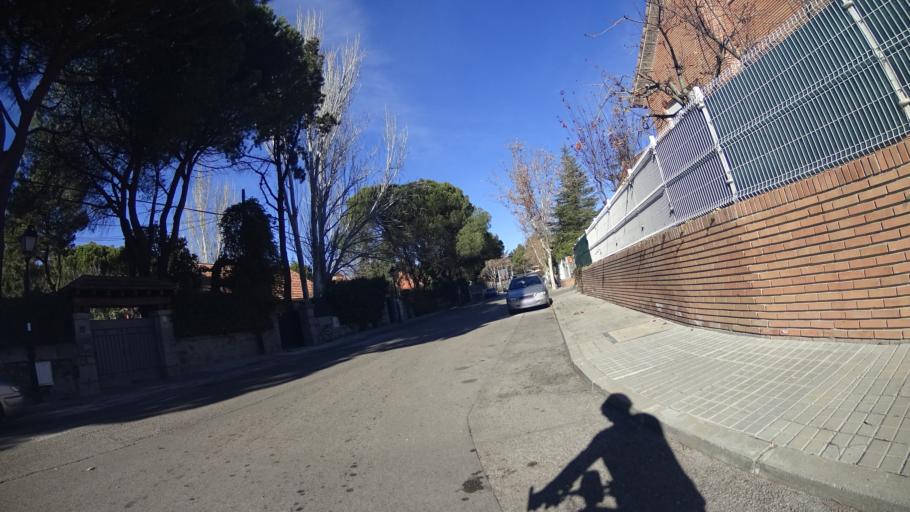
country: ES
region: Madrid
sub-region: Provincia de Madrid
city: Torrelodones
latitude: 40.5743
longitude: -3.9515
